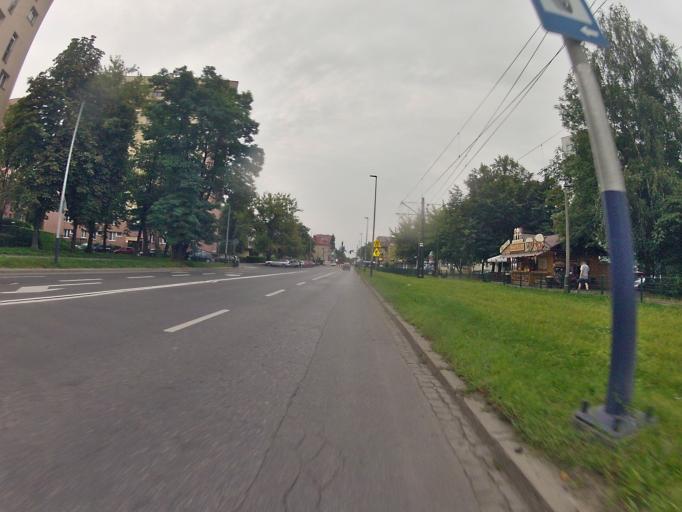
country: PL
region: Lesser Poland Voivodeship
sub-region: Krakow
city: Krakow
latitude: 50.0799
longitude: 19.8953
